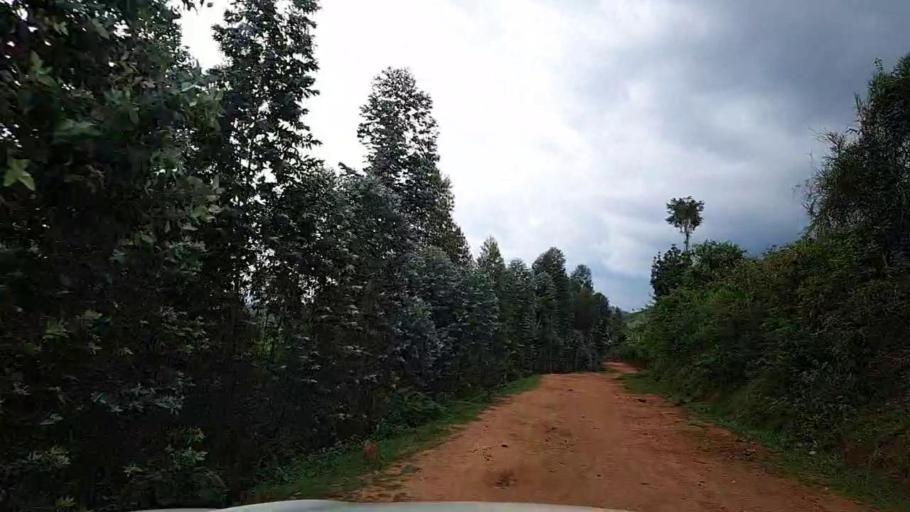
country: RW
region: Southern Province
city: Gikongoro
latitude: -2.4162
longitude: 29.6601
